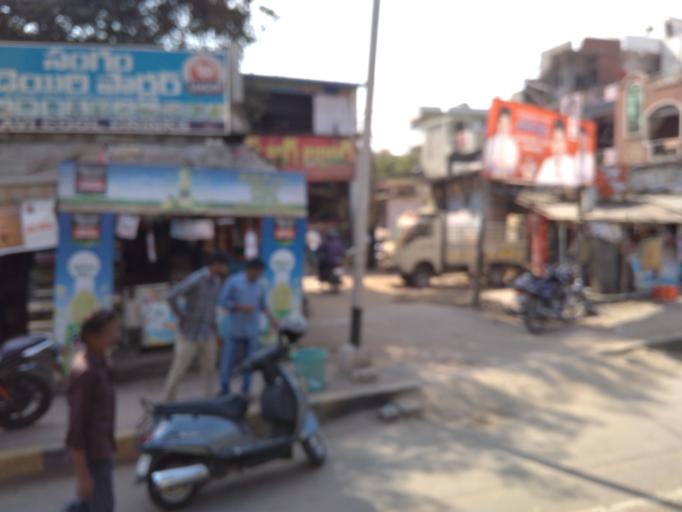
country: IN
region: Andhra Pradesh
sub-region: Krishna
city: Yanamalakuduru
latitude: 16.5239
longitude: 80.6850
